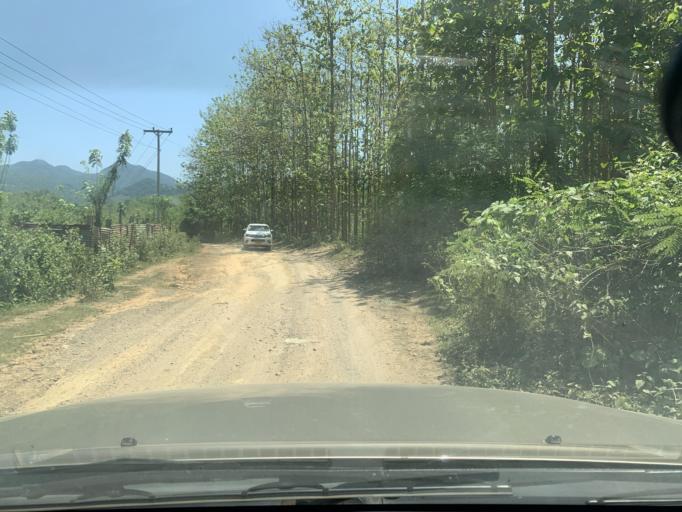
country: LA
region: Louangphabang
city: Louangphabang
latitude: 19.9050
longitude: 102.2419
